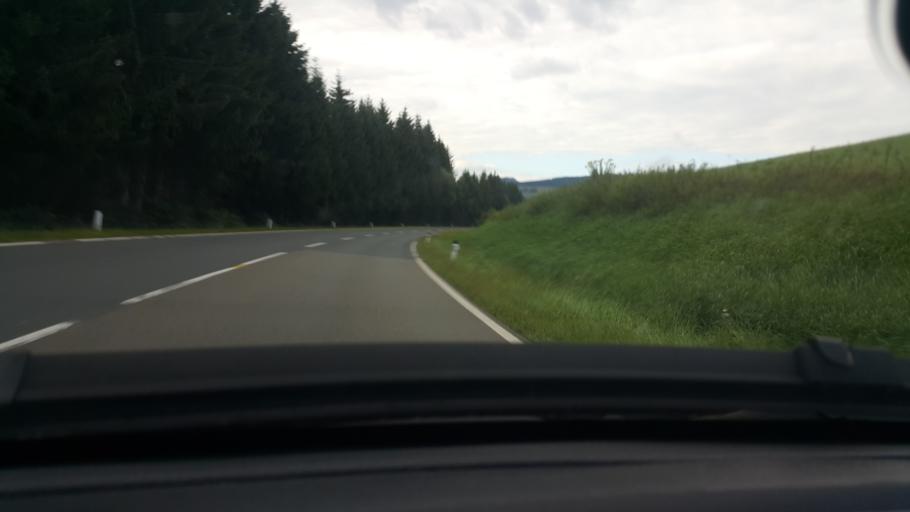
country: AT
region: Carinthia
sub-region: Politischer Bezirk Feldkirchen
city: Feldkirchen in Karnten
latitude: 46.7012
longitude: 14.1195
